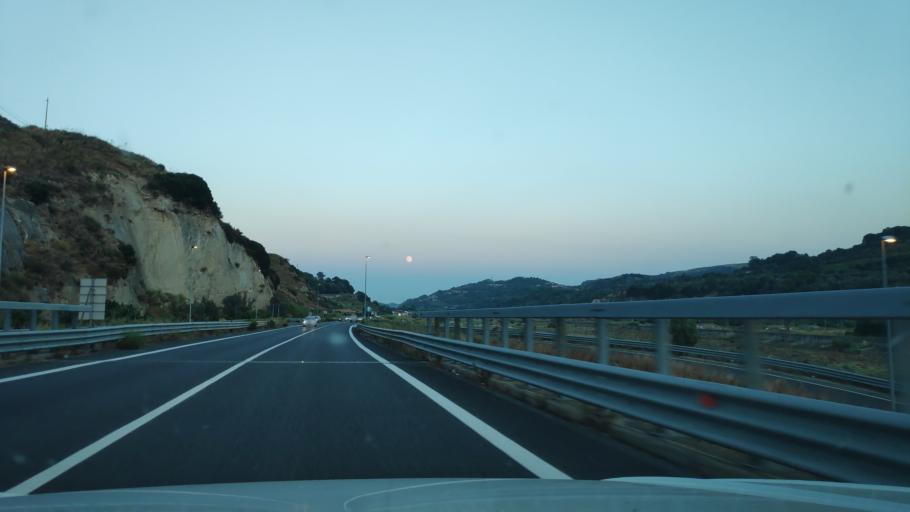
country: IT
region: Calabria
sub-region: Provincia di Reggio Calabria
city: Mammola
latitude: 38.3560
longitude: 16.2399
